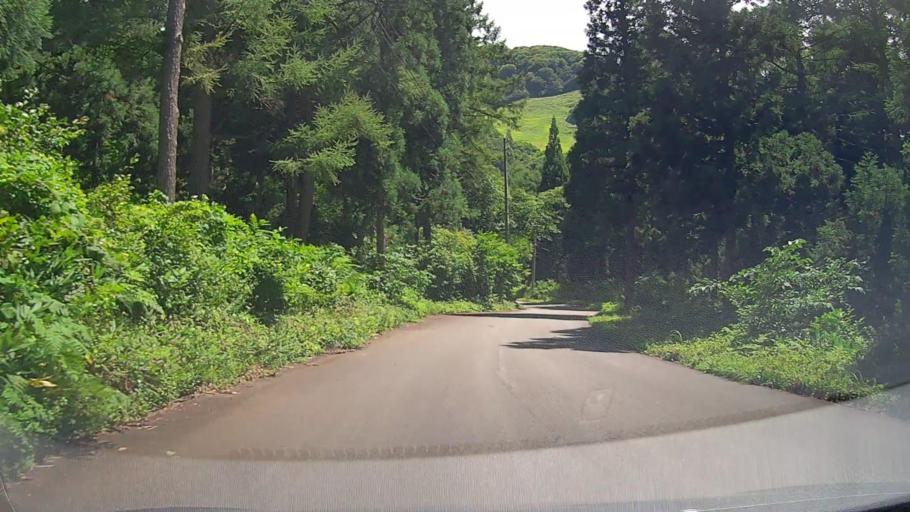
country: JP
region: Nagano
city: Iiyama
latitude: 36.9324
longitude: 138.4612
